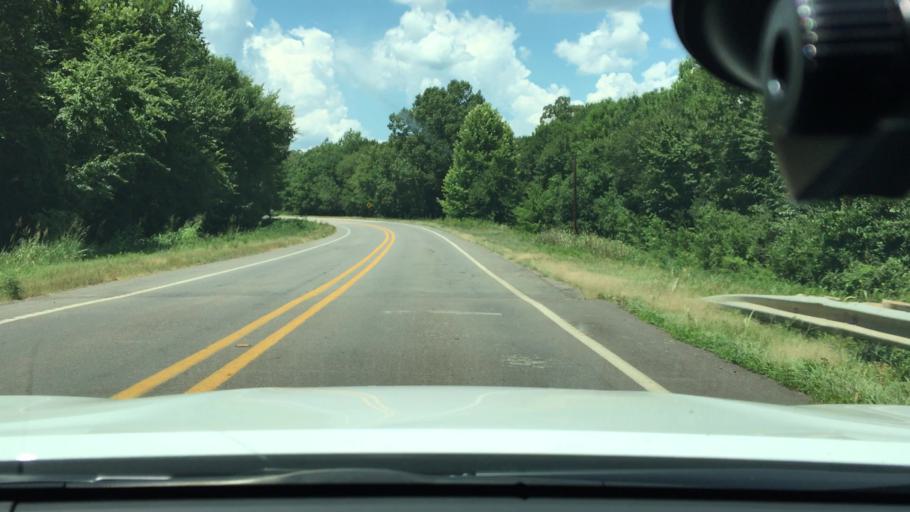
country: US
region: Arkansas
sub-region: Logan County
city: Booneville
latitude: 35.1504
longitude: -93.8297
